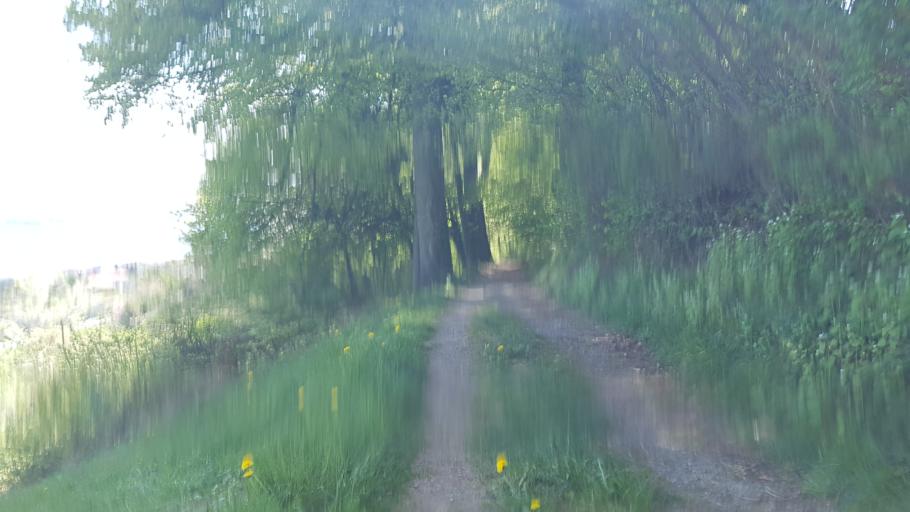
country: CH
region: Aargau
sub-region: Bezirk Lenzburg
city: Boniswil
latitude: 47.2926
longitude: 8.1901
